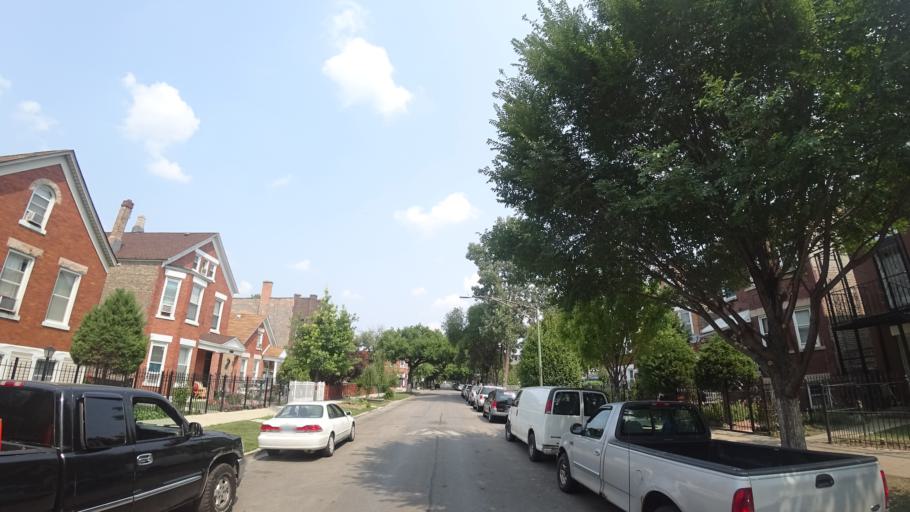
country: US
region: Illinois
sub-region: Cook County
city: Cicero
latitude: 41.8399
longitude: -87.7183
